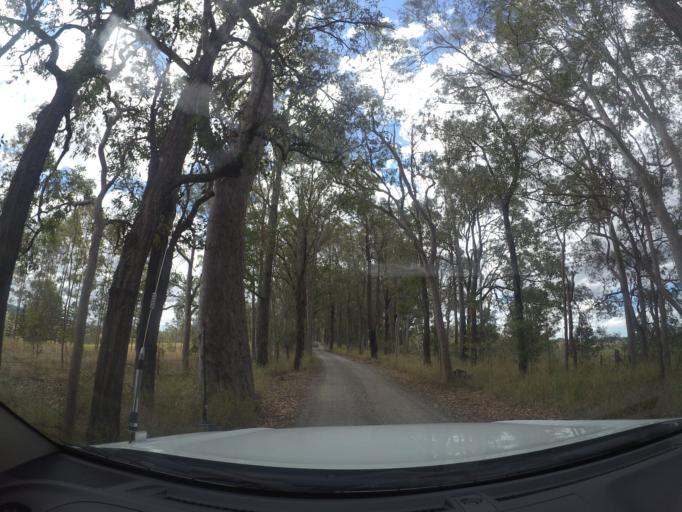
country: AU
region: Queensland
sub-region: Logan
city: Cedar Vale
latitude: -27.9119
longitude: 153.0313
